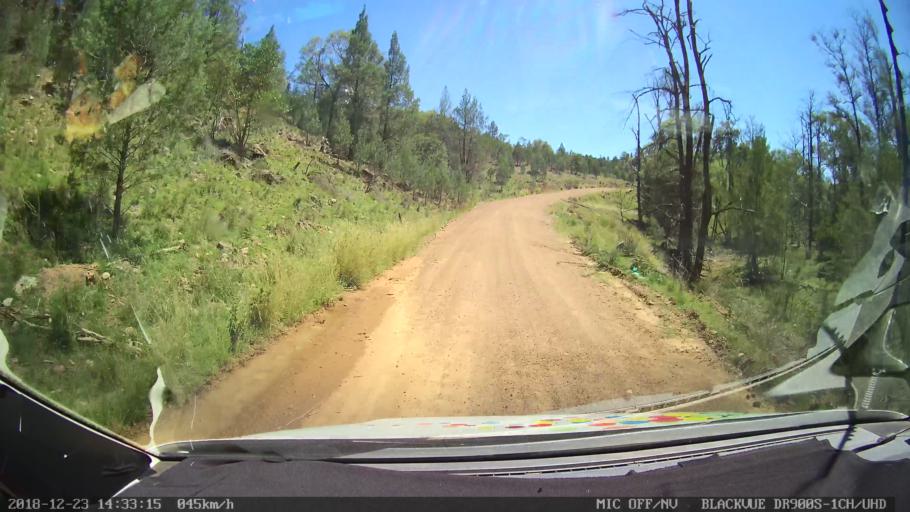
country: AU
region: New South Wales
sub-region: Tamworth Municipality
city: Manilla
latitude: -30.6071
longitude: 150.9146
